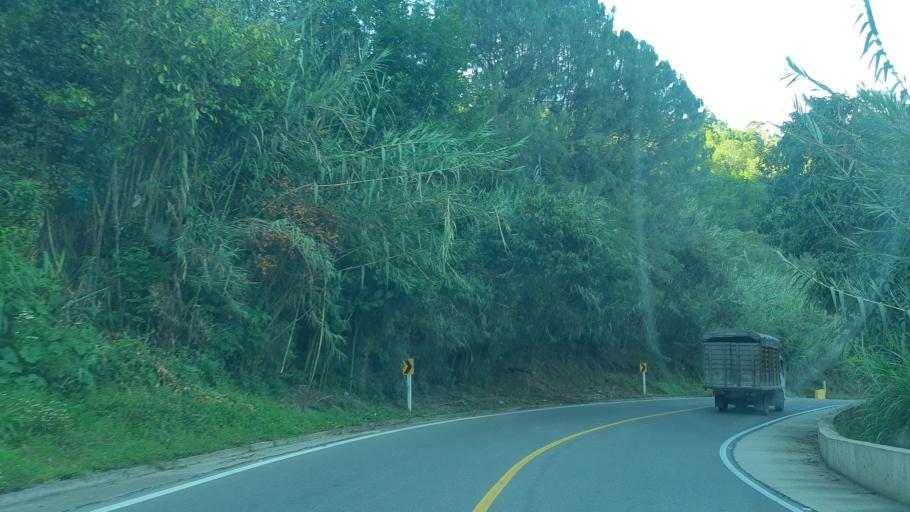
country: CO
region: Boyaca
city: Guateque
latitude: 5.0066
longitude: -73.4968
